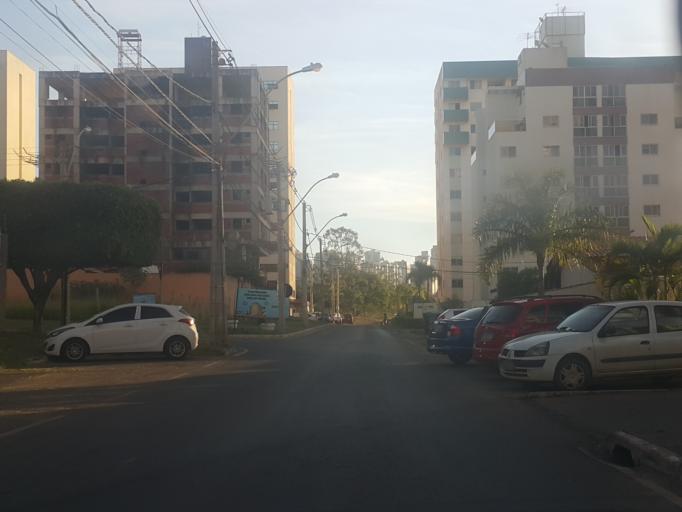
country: BR
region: Federal District
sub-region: Brasilia
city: Brasilia
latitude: -15.8301
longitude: -48.0167
